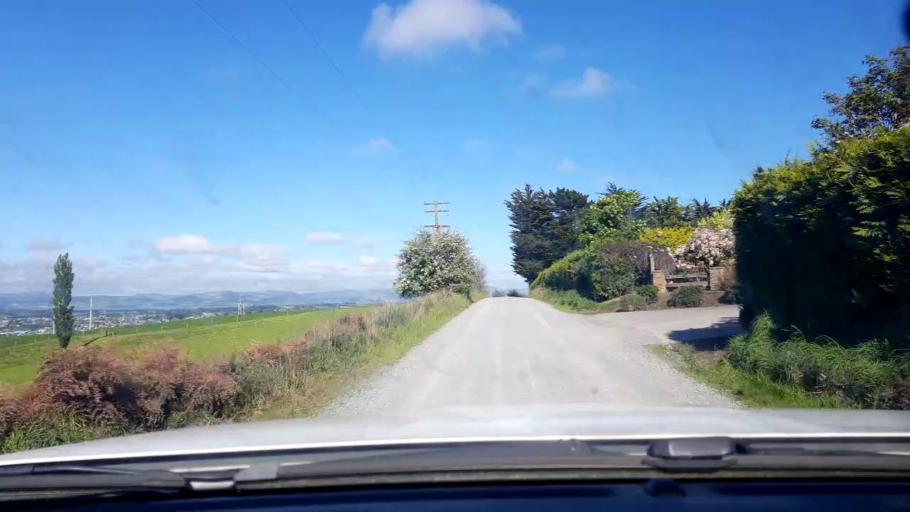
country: NZ
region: Otago
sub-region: Clutha District
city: Balclutha
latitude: -46.2234
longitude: 169.7597
